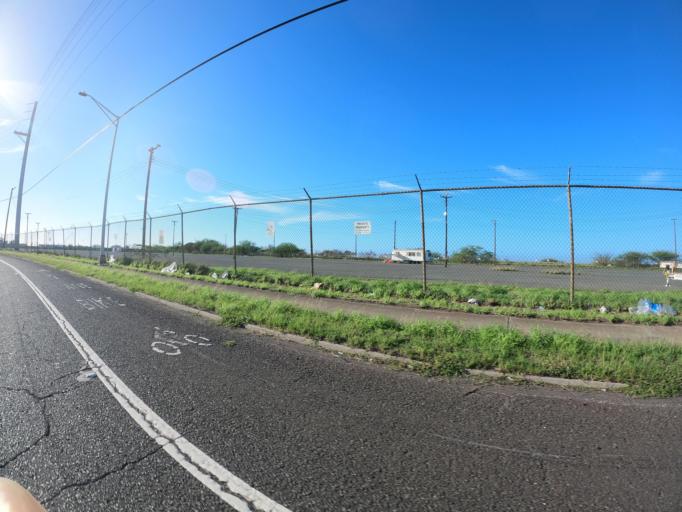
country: US
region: Hawaii
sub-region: Honolulu County
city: Honolulu
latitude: 21.3086
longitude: -157.8857
